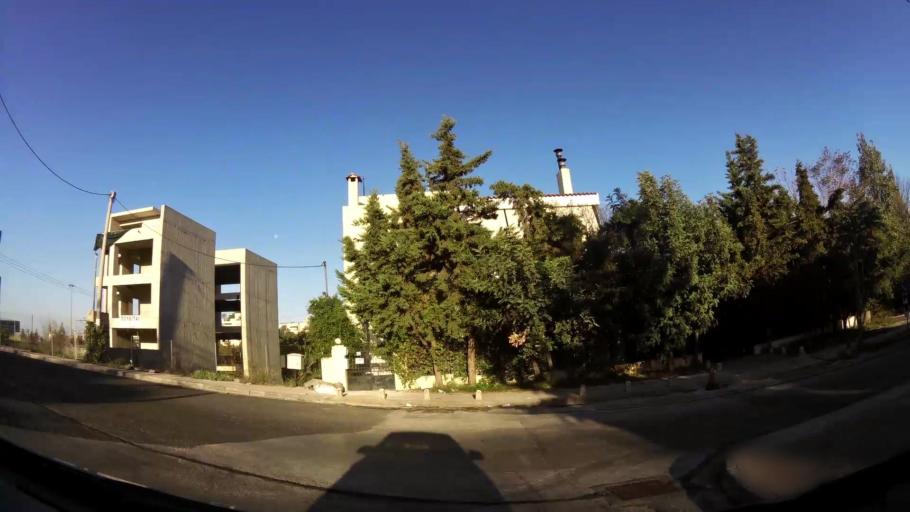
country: GR
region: Attica
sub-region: Nomarchia Athinas
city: Marousi
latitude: 38.0442
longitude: 23.8021
